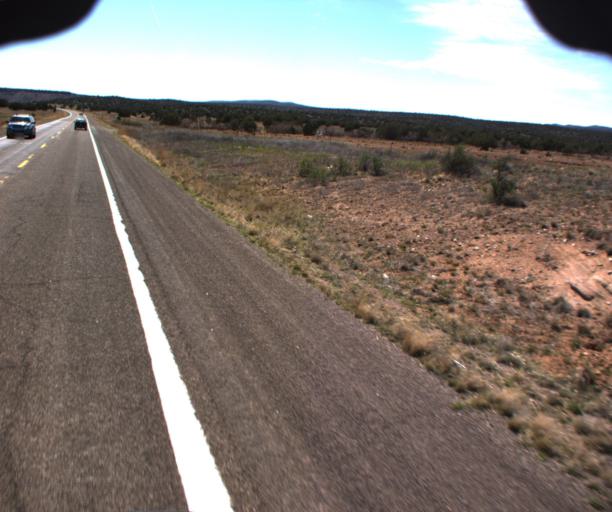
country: US
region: Arizona
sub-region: Mohave County
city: Peach Springs
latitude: 35.4548
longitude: -113.6254
